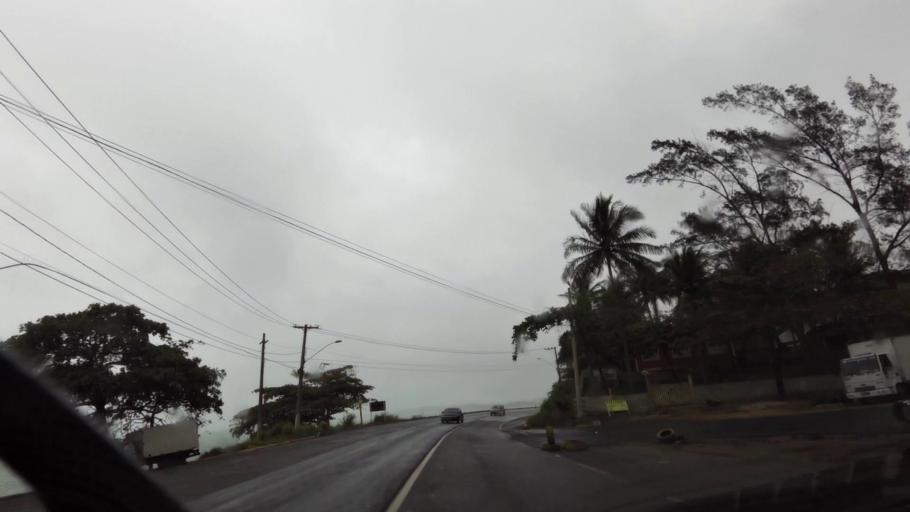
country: BR
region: Espirito Santo
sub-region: Guarapari
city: Guarapari
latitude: -20.7380
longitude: -40.5435
